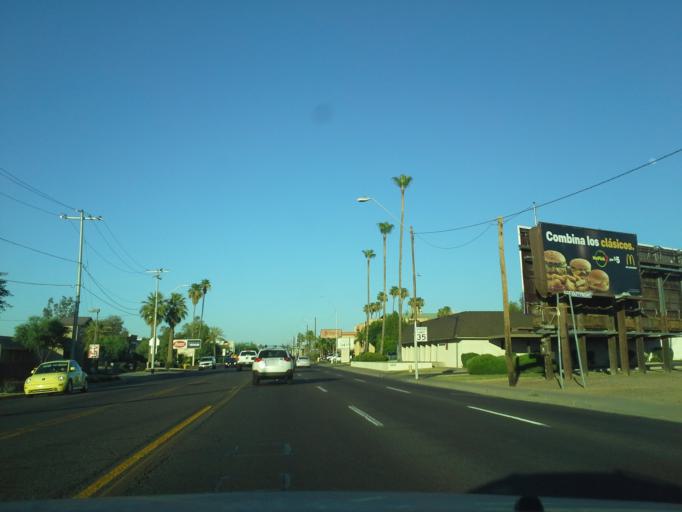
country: US
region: Arizona
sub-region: Maricopa County
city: Phoenix
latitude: 33.4803
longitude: -112.0337
